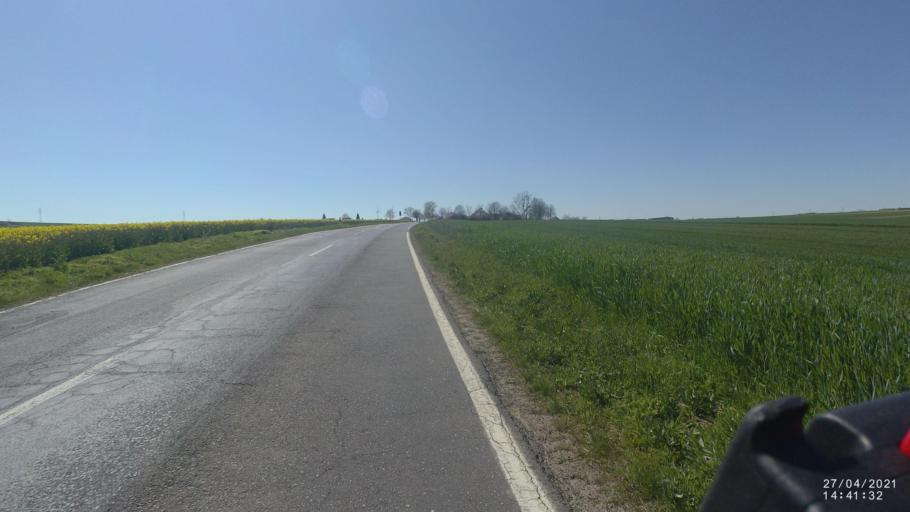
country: DE
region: Rheinland-Pfalz
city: Kollig
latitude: 50.2674
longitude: 7.2854
